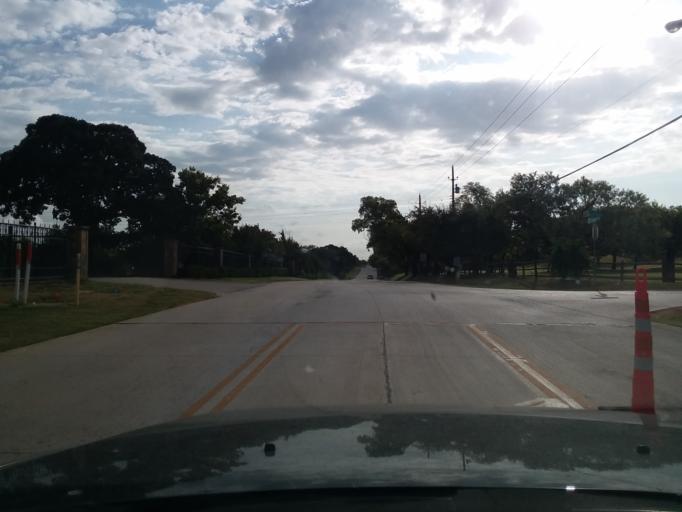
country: US
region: Texas
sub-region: Denton County
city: Hickory Creek
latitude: 33.1227
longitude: -97.0526
